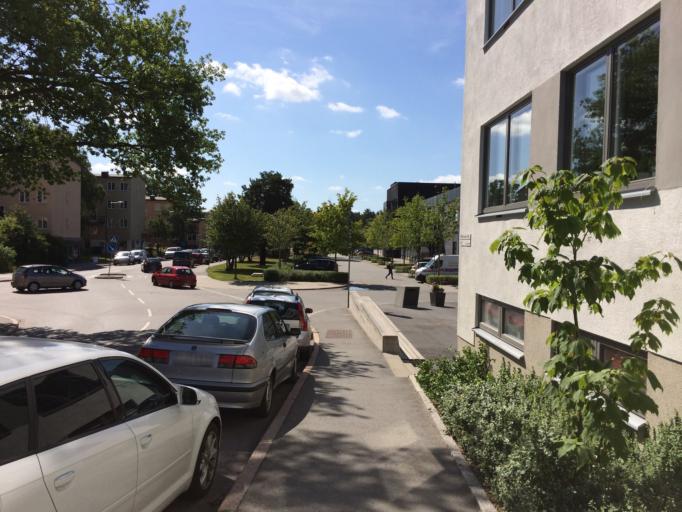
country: SE
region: Stockholm
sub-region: Stockholms Kommun
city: Arsta
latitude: 59.3004
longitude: 17.9950
